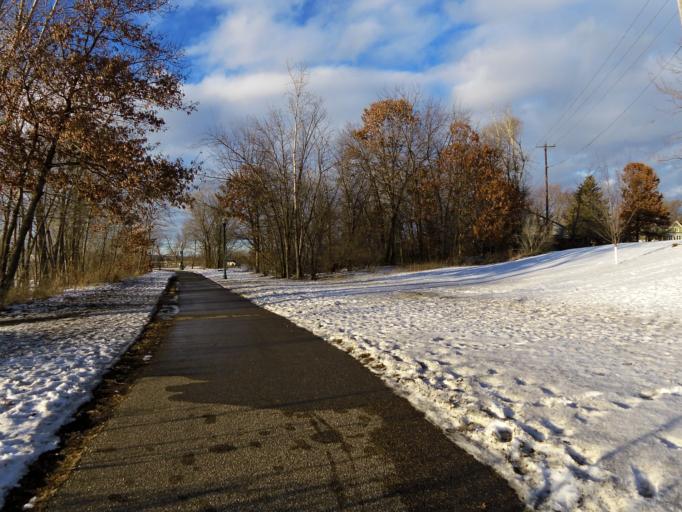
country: US
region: Wisconsin
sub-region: Saint Croix County
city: Hudson
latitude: 44.9813
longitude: -92.7598
